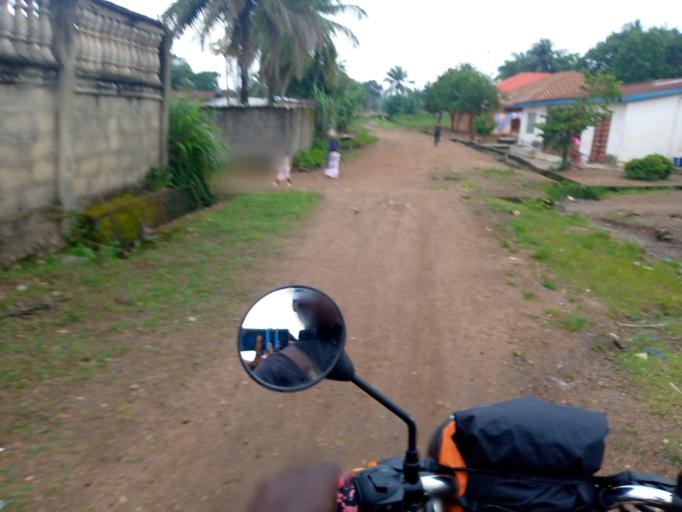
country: SL
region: Eastern Province
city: Kenema
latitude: 7.8650
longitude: -11.1938
